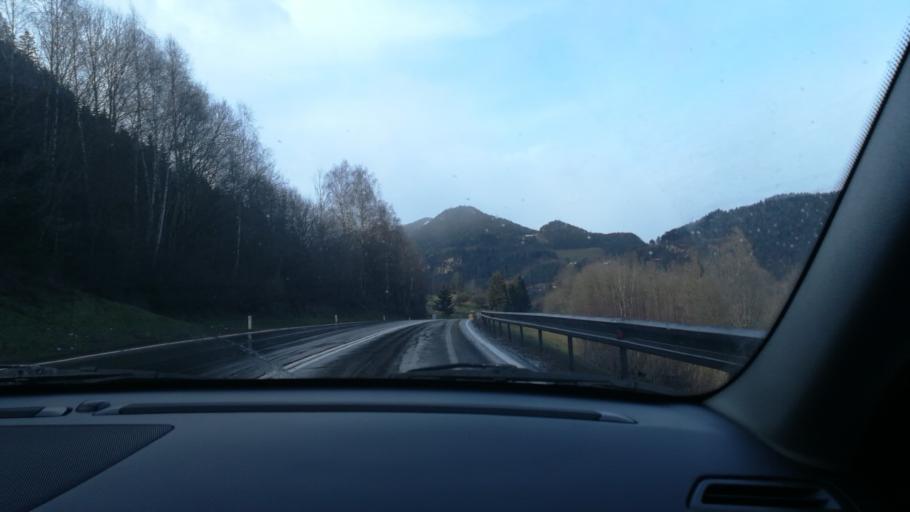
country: AT
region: Styria
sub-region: Politischer Bezirk Murtal
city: Sankt Peter ob Judenburg
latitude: 47.1969
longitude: 14.5728
